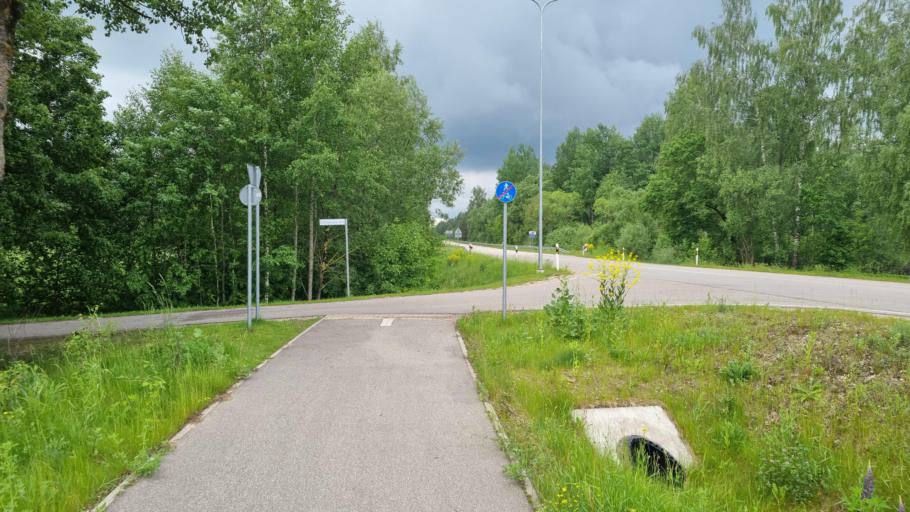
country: LV
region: Daugavpils
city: Daugavpils
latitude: 55.9039
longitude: 26.6469
